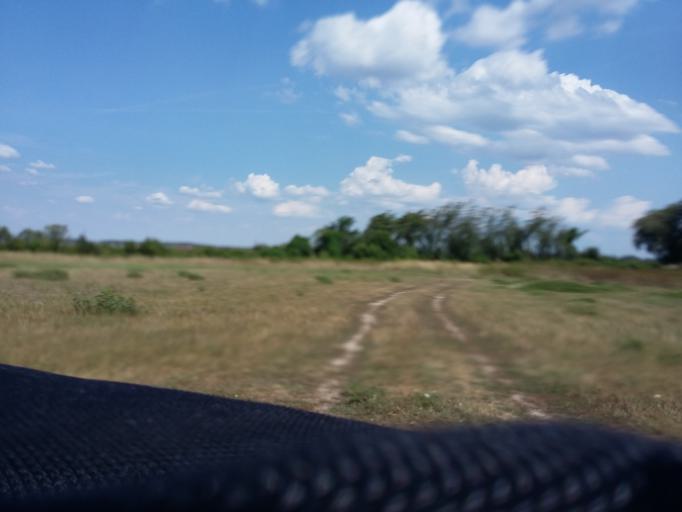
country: SK
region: Bratislavsky
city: Stupava
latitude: 48.3202
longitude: 17.0352
